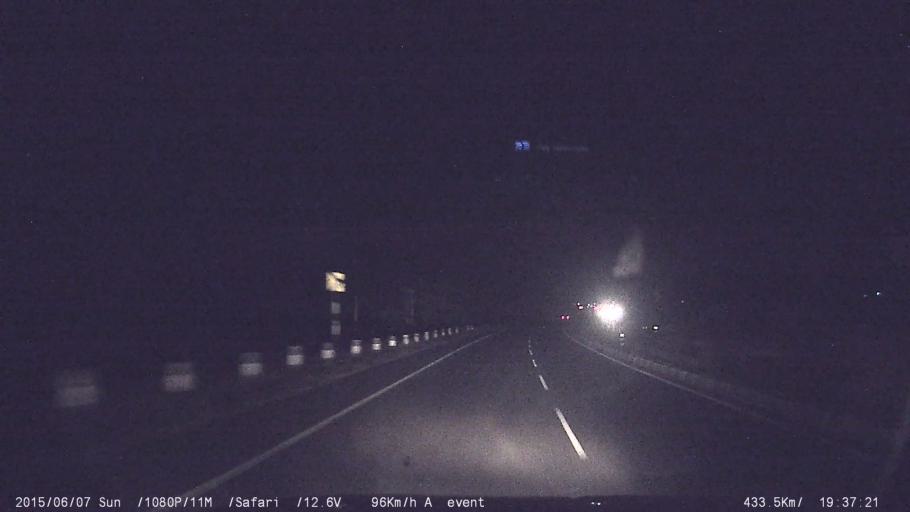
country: IN
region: Tamil Nadu
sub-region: Erode
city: Perundurai
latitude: 11.3410
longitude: 77.6317
